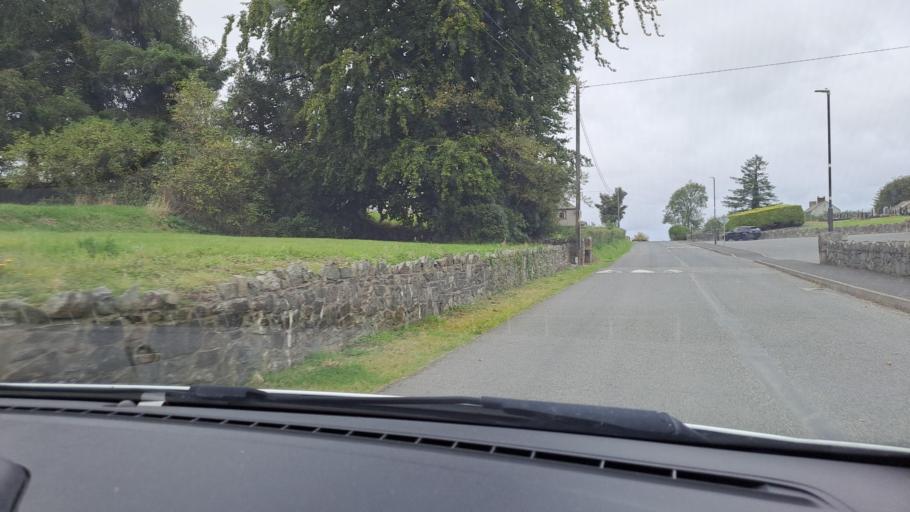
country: IE
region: Ulster
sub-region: An Cabhan
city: Kingscourt
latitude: 54.0122
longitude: -6.8209
